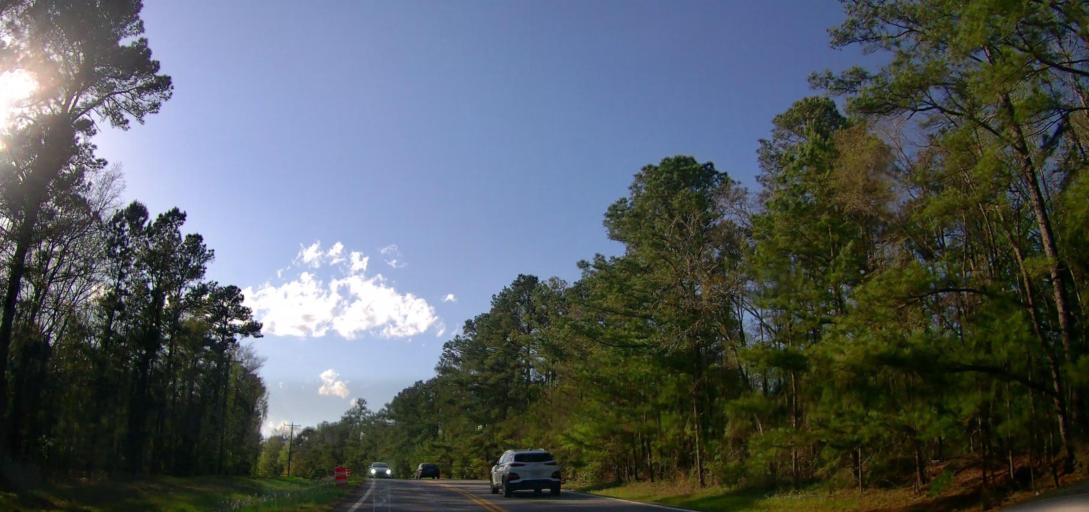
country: US
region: Georgia
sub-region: Baldwin County
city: Milledgeville
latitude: 33.1267
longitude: -83.2988
